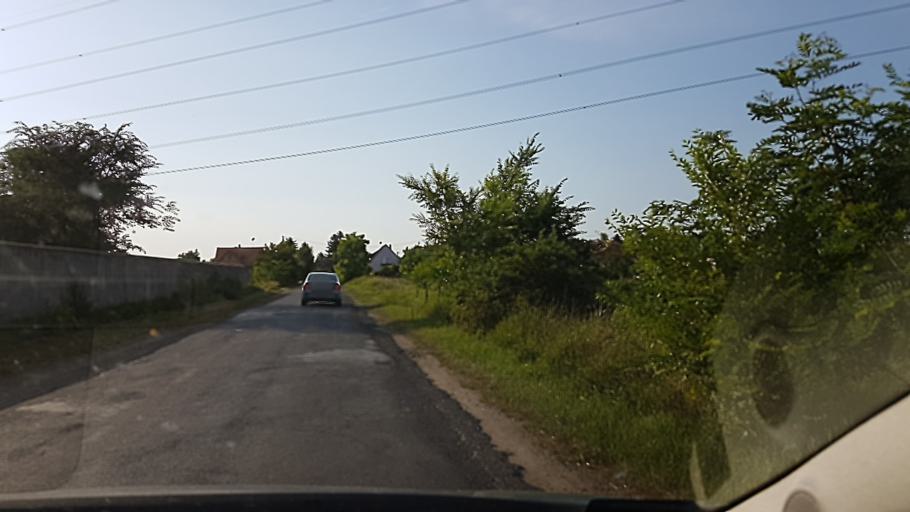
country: HU
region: Pest
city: Delegyhaza
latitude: 47.2452
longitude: 19.0687
